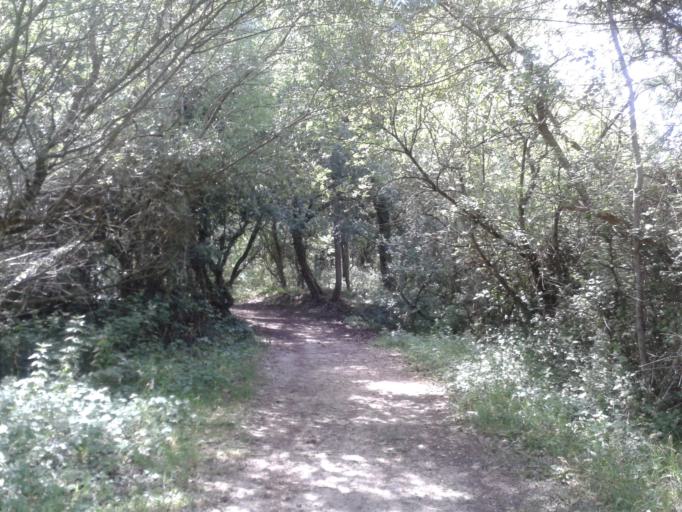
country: FR
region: Picardie
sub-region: Departement de la Somme
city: Fort-Mahon-Plage
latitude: 50.3527
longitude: 1.5658
